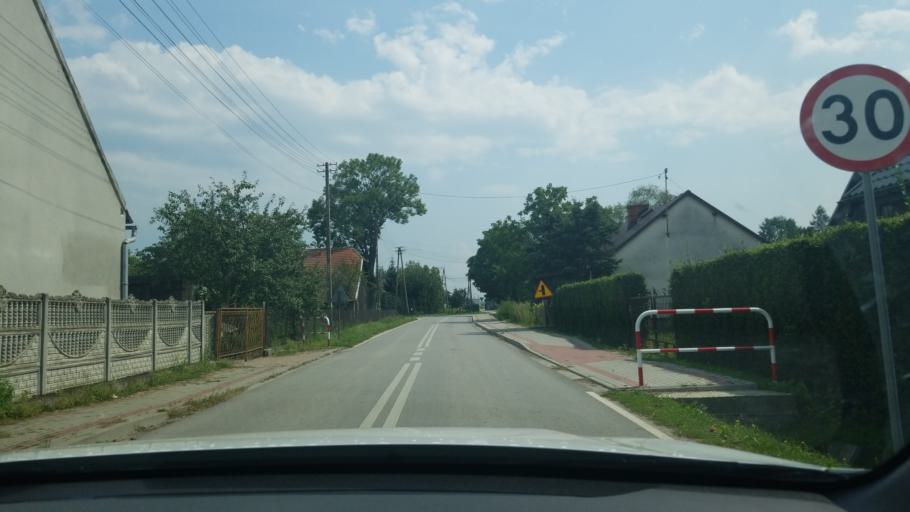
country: PL
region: Lesser Poland Voivodeship
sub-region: Powiat bochenski
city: Dziewin
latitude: 50.1167
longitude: 20.5156
